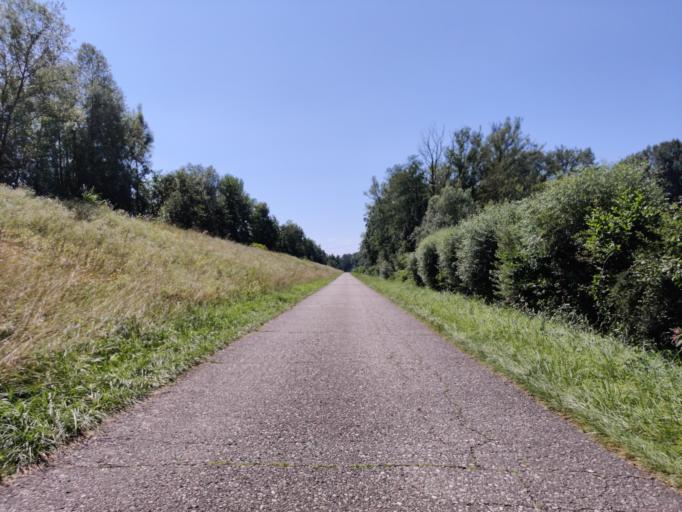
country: AT
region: Styria
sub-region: Politischer Bezirk Leibnitz
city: Gabersdorf
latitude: 46.7913
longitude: 15.5839
